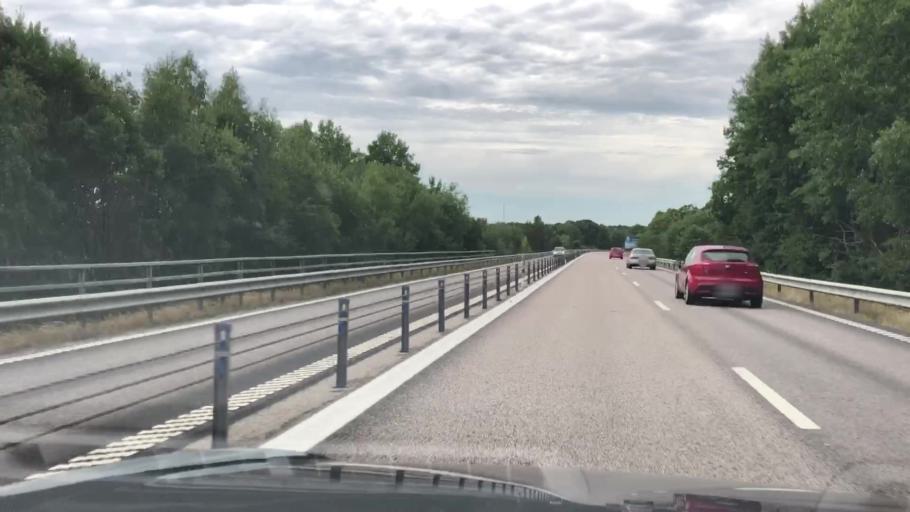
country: SE
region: Blekinge
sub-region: Karlshamns Kommun
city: Karlshamn
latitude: 56.1943
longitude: 14.9668
